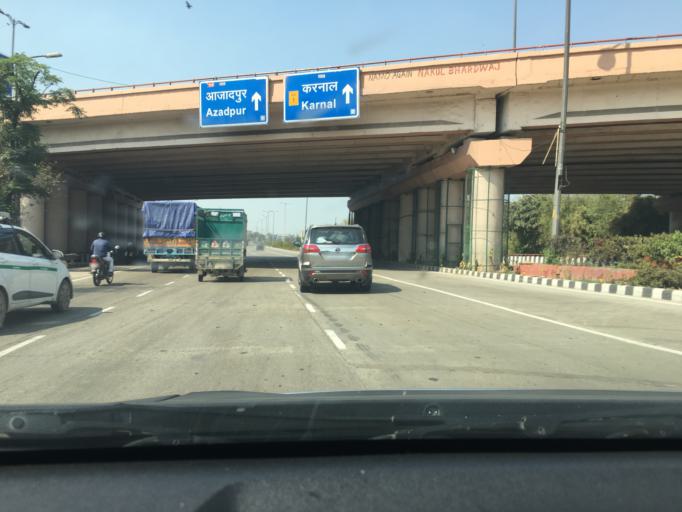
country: IN
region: NCT
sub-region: North Delhi
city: Delhi
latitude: 28.6509
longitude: 77.2516
